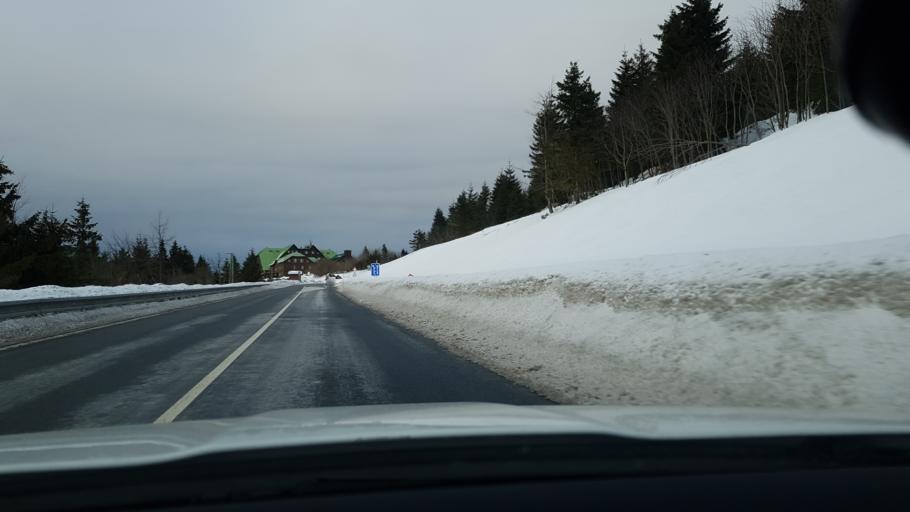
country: CZ
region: Olomoucky
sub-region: Okres Sumperk
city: Loucna nad Desnou
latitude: 50.1220
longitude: 17.1508
